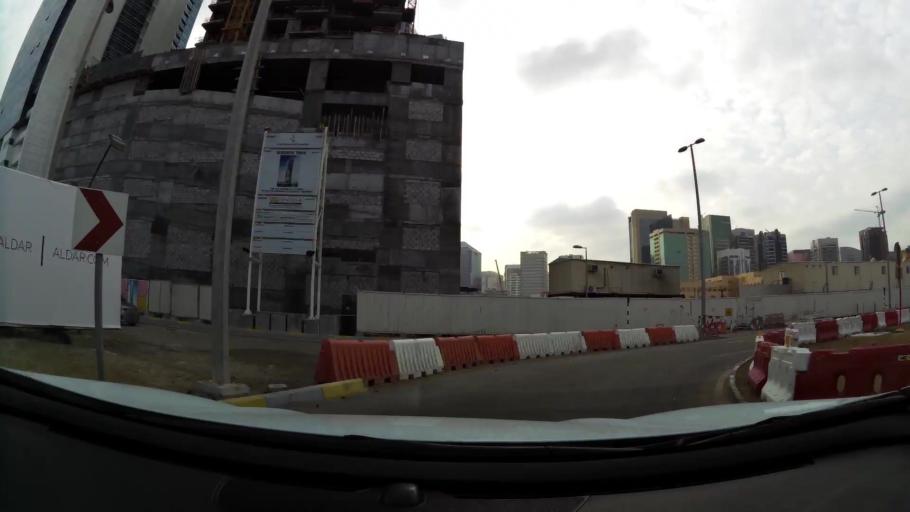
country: AE
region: Abu Dhabi
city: Abu Dhabi
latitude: 24.5036
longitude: 54.3685
